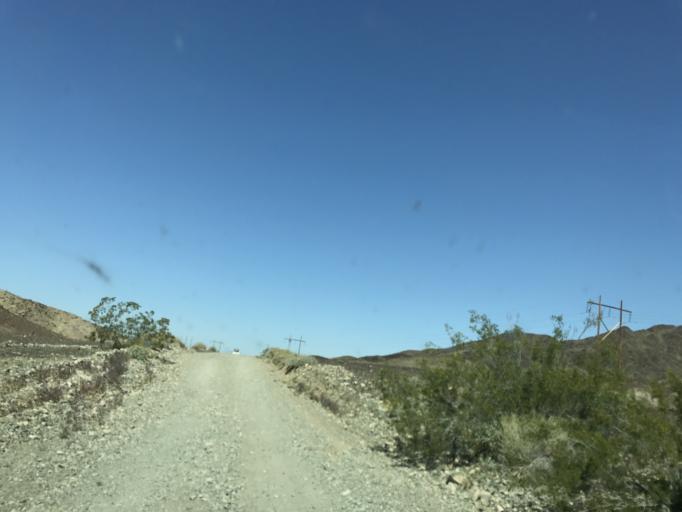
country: US
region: California
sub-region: Riverside County
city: Mesa Verde
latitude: 33.4961
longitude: -114.8359
